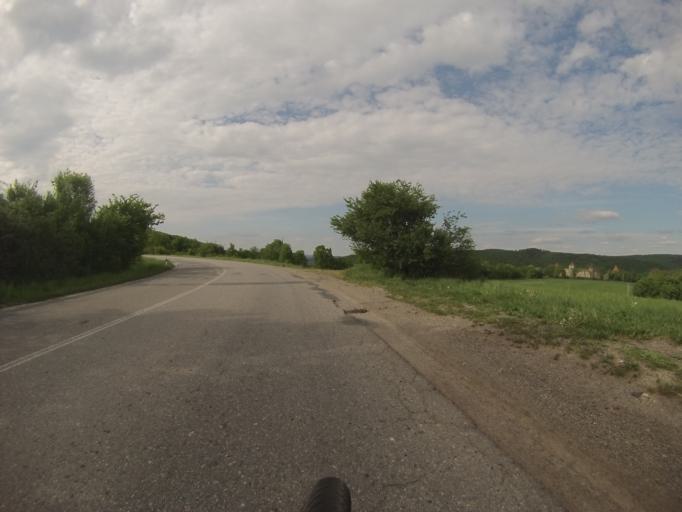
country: CZ
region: South Moravian
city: Veverska Bityska
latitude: 49.2536
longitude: 16.4551
